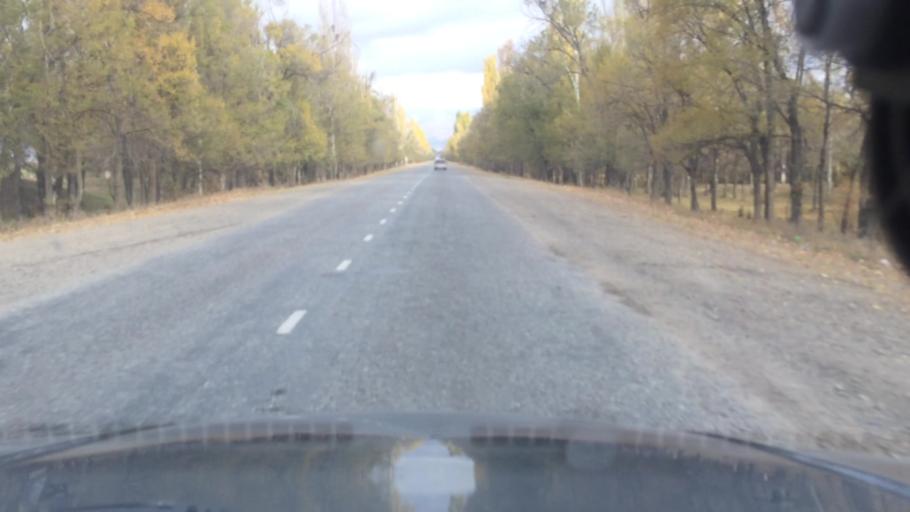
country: KG
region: Ysyk-Koel
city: Tyup
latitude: 42.6313
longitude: 78.3604
